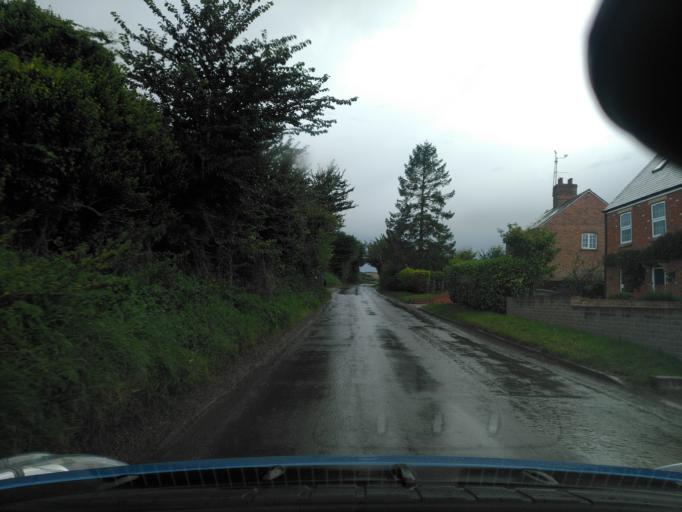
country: GB
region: England
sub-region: Borough of Swindon
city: Bishopstone
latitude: 51.5559
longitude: -1.6321
